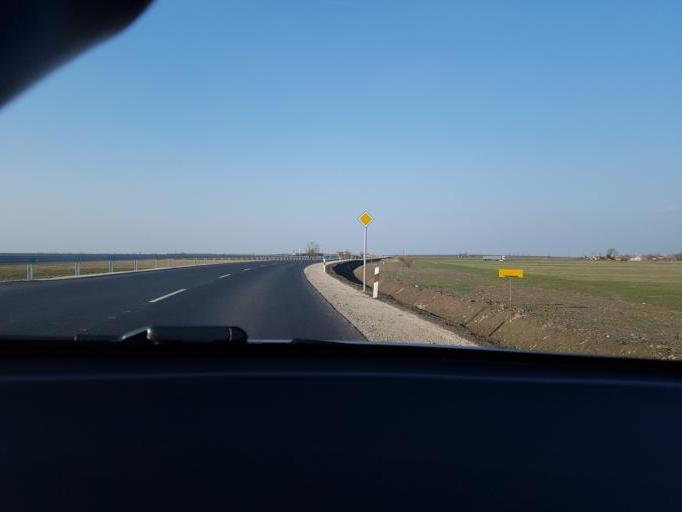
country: RO
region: Arad
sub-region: Comuna Nadlac
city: Nadlac
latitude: 46.1934
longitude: 20.7135
